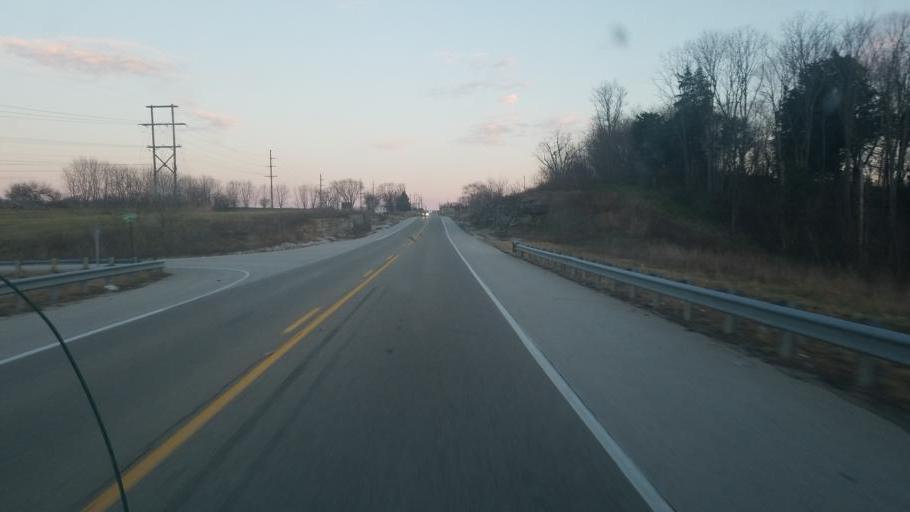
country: US
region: Indiana
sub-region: Lawrence County
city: Bedford
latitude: 38.8752
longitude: -86.3813
